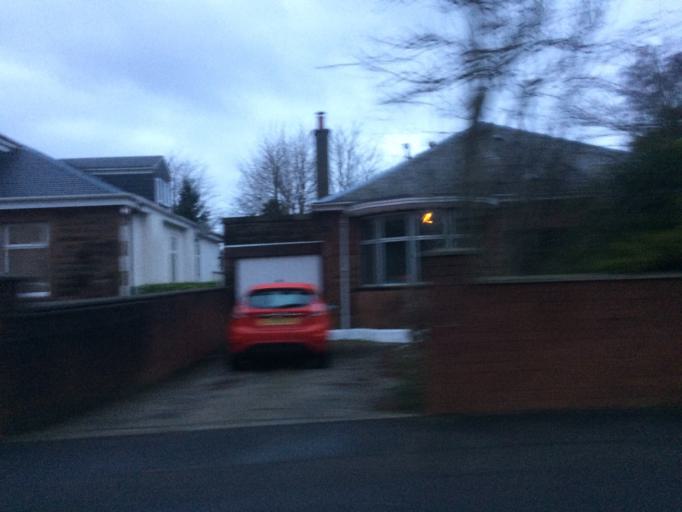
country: GB
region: Scotland
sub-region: East Renfrewshire
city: Newton Mearns
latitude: 55.7773
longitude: -4.3255
